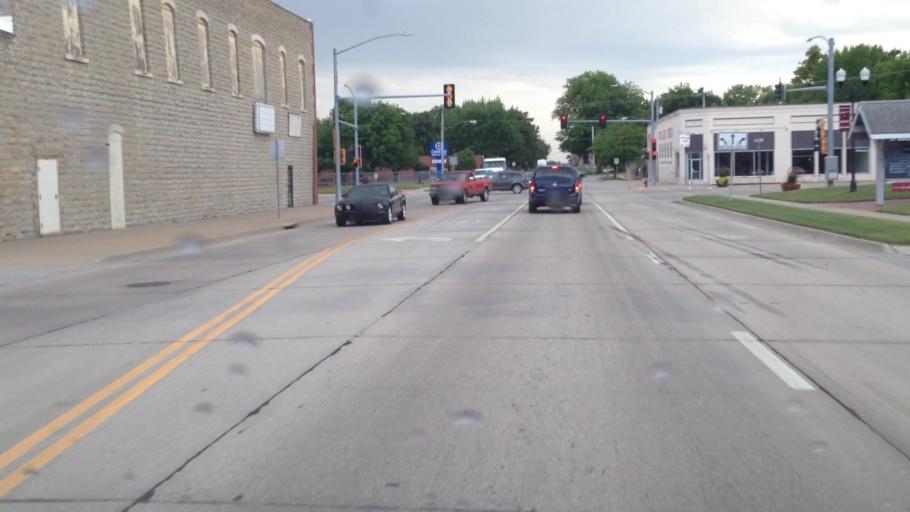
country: US
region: Kansas
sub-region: Coffey County
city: Burlington
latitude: 38.1954
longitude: -95.7387
